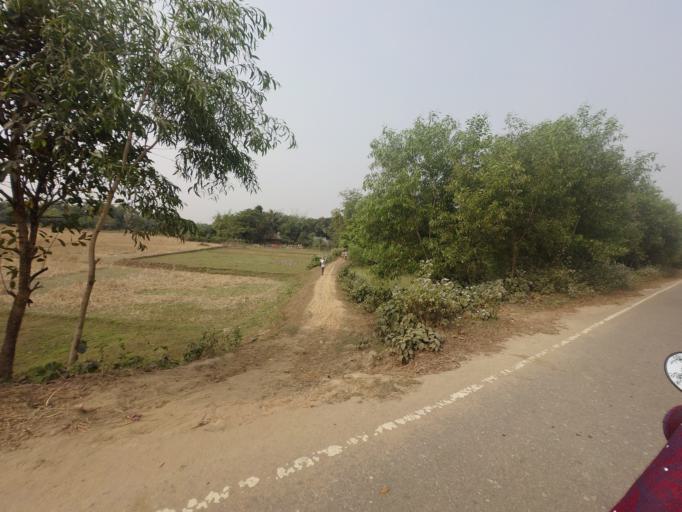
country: BD
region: Dhaka
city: Netrakona
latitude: 25.1377
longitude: 90.6613
